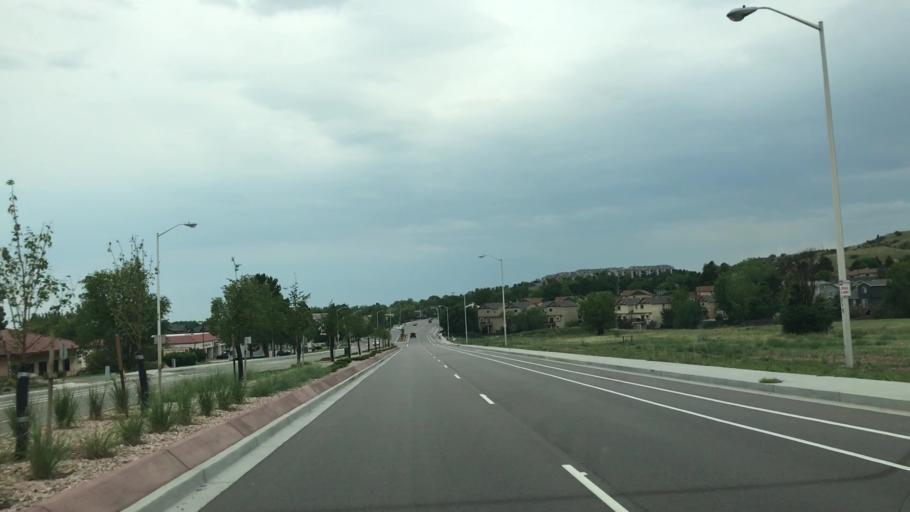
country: US
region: Colorado
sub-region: El Paso County
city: Colorado Springs
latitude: 38.8929
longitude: -104.8512
